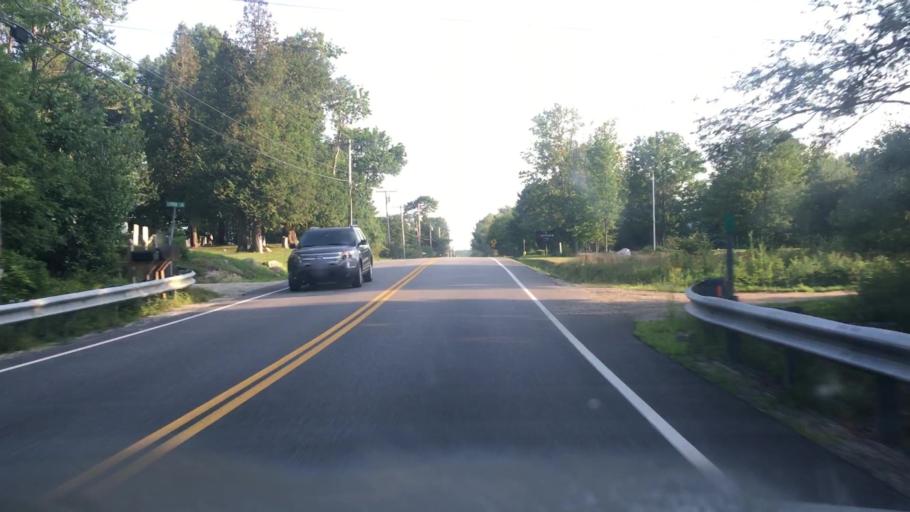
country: US
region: Maine
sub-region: Cumberland County
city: Freeport
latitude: 43.9081
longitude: -70.0920
